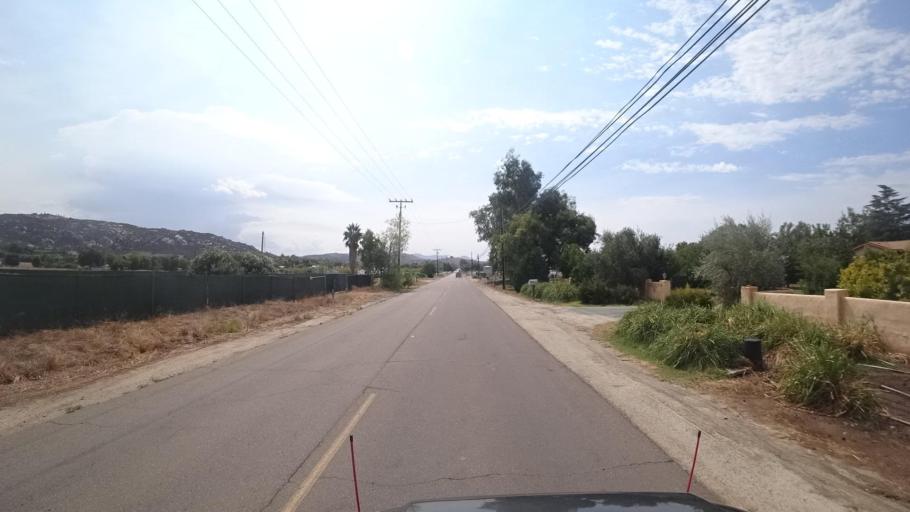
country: US
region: California
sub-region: San Diego County
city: Ramona
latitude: 33.0672
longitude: -116.8452
